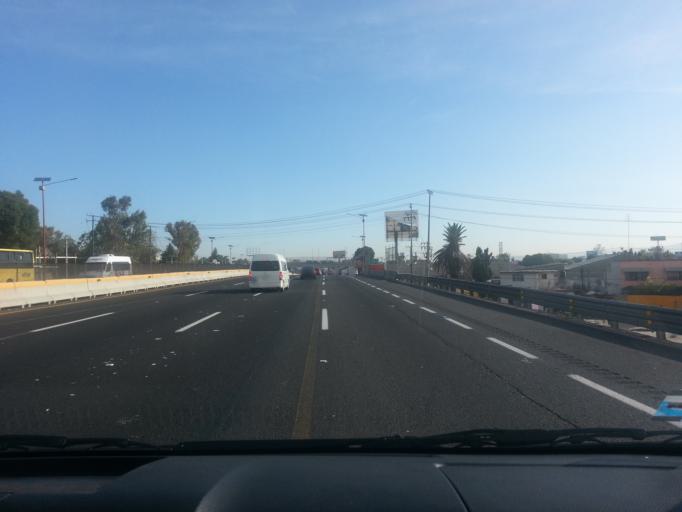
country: MX
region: Mexico
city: Ecatepec
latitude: 19.5935
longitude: -99.0405
